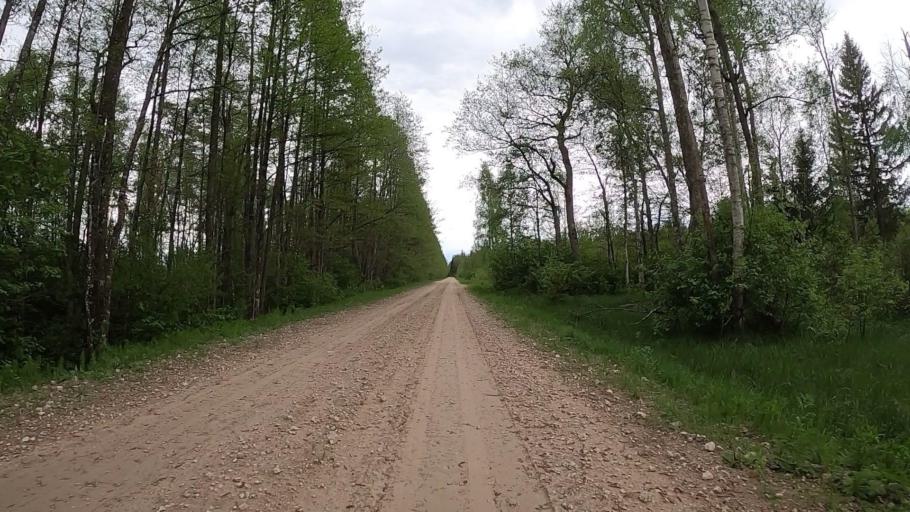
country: LV
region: Ozolnieku
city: Ozolnieki
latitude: 56.7823
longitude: 23.7691
